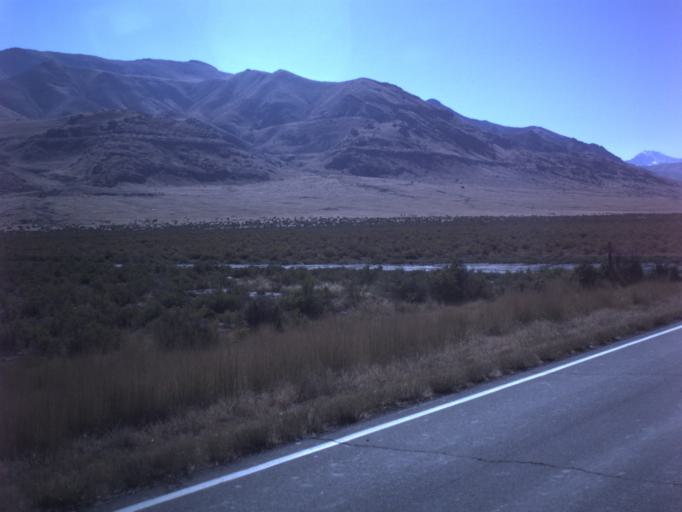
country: US
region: Utah
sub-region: Tooele County
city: Grantsville
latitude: 40.7125
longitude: -112.6625
